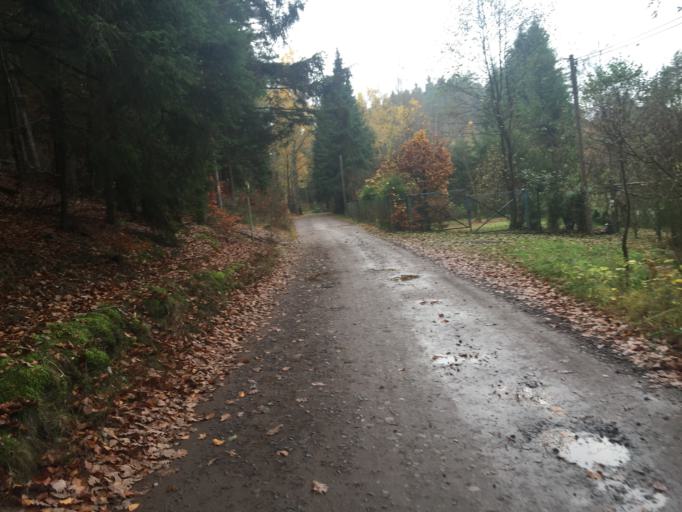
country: DE
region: Rheinland-Pfalz
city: Carlsberg
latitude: 49.4885
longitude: 8.0220
